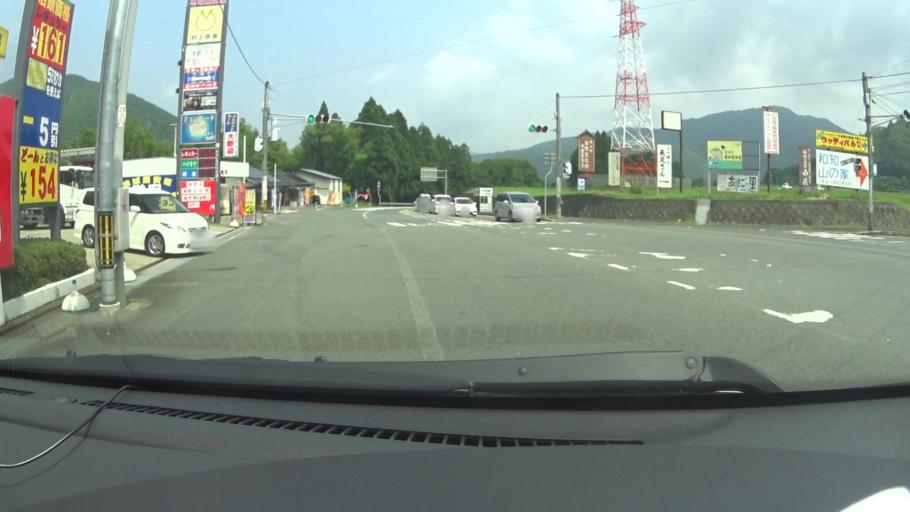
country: JP
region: Kyoto
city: Ayabe
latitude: 35.2487
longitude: 135.4187
